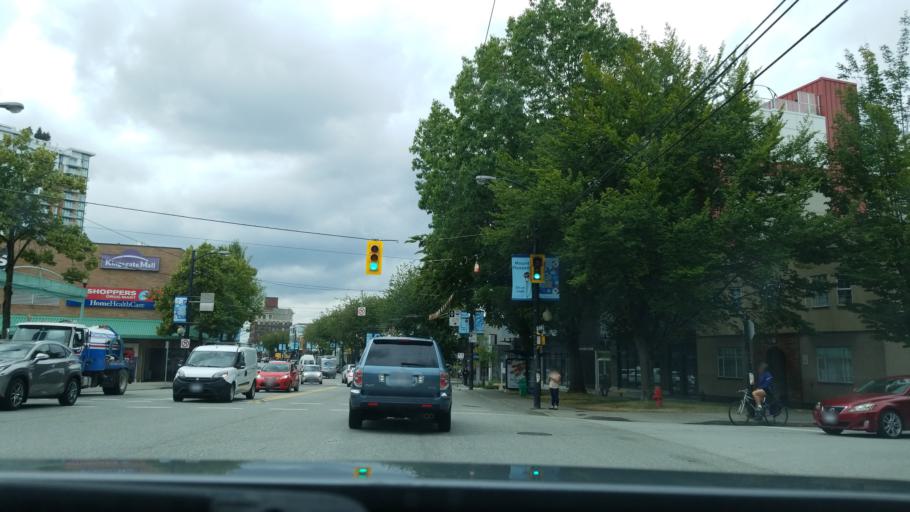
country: CA
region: British Columbia
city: Vancouver
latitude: 49.2626
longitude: -123.0958
